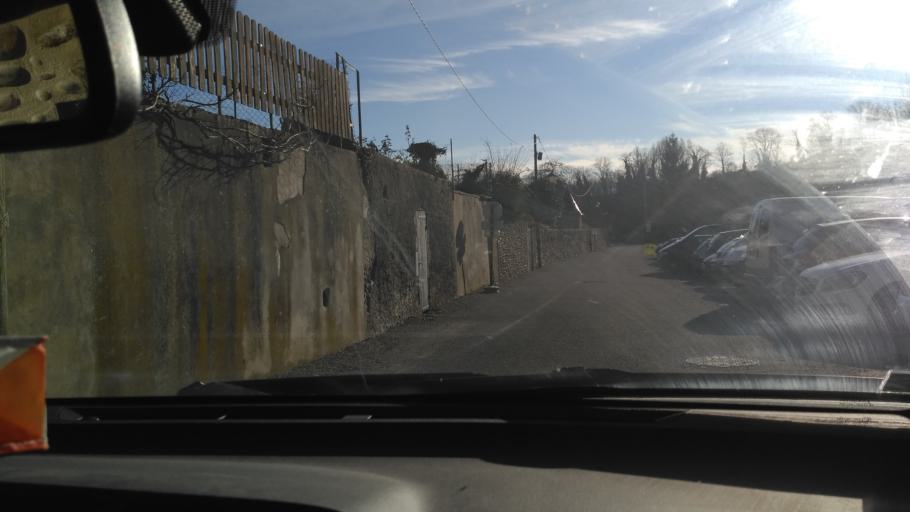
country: FR
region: Rhone-Alpes
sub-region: Departement de l'Isere
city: Saint-Antoine-l'Abbaye
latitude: 45.1741
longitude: 5.2163
